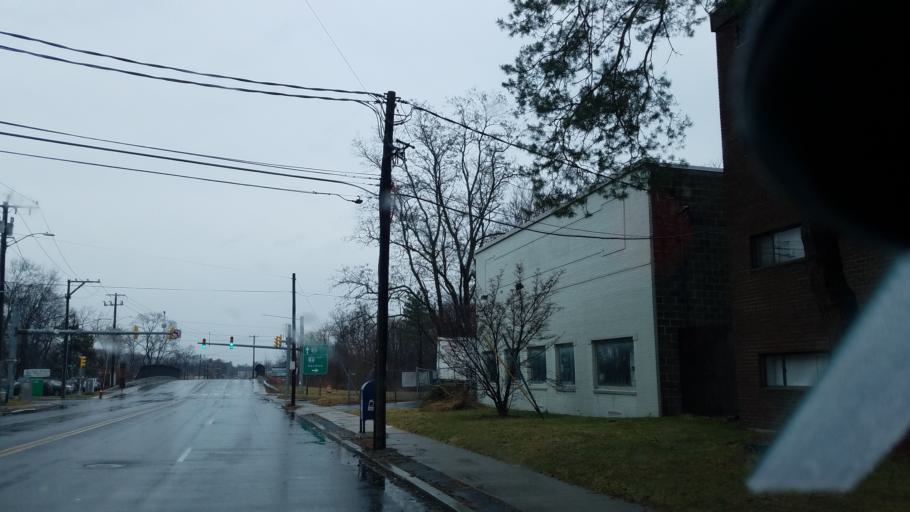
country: US
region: Connecticut
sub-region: Hartford County
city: West Hartford
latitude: 41.7485
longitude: -72.7151
